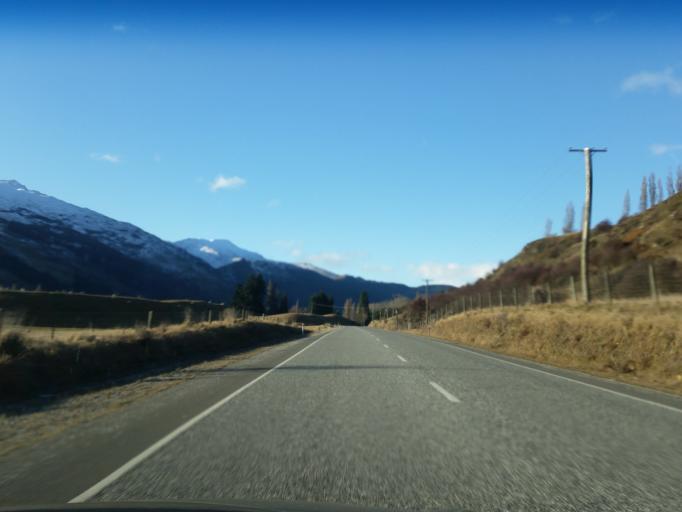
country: NZ
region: Otago
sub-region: Queenstown-Lakes District
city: Queenstown
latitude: -44.9636
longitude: 168.7166
